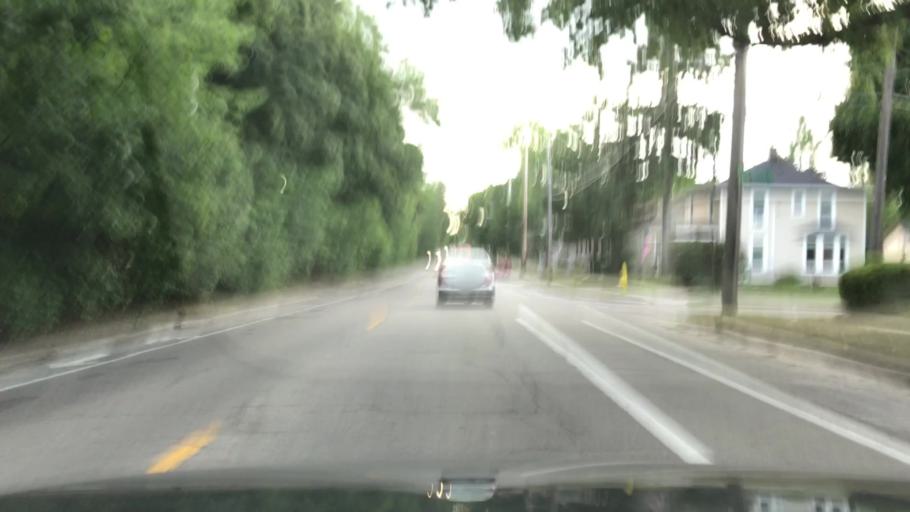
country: US
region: Michigan
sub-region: Kent County
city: Grand Rapids
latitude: 42.9990
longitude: -85.6519
